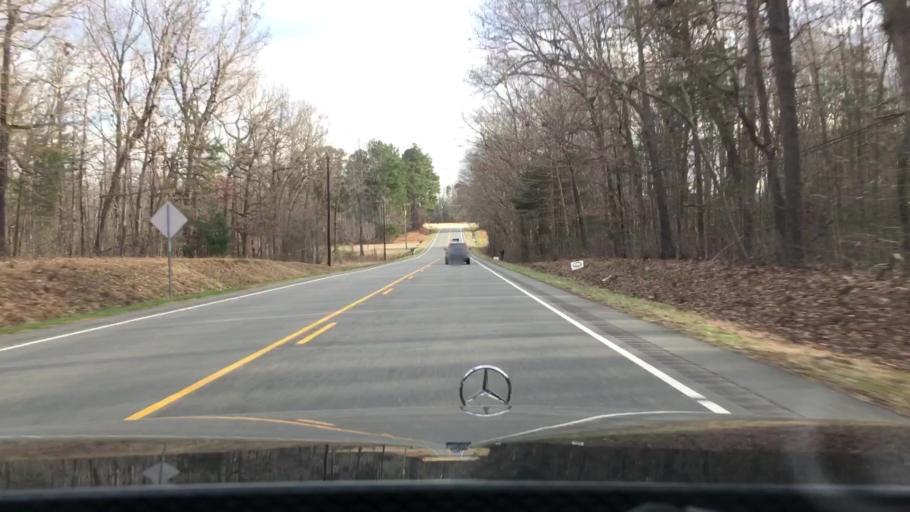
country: US
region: North Carolina
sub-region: Orange County
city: Hillsborough
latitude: 36.1934
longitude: -79.1401
